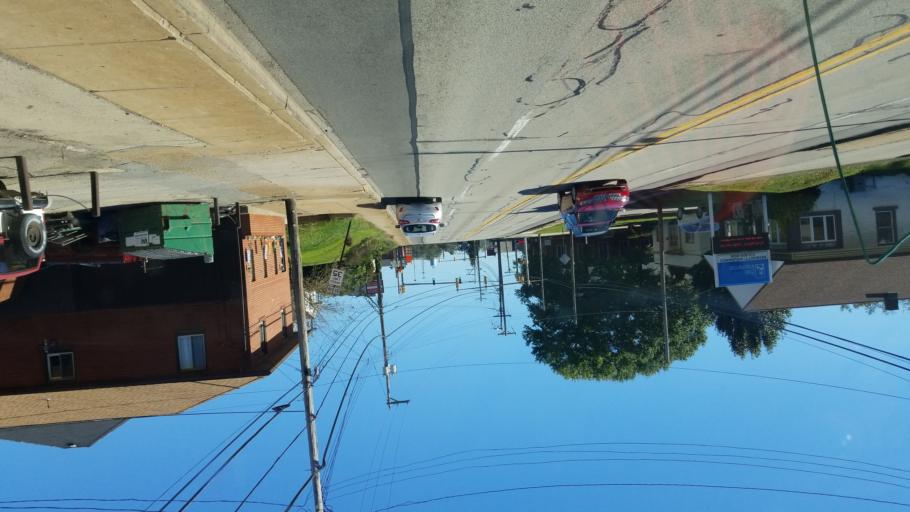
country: US
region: Pennsylvania
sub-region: Allegheny County
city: North Versailles
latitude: 40.3795
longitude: -79.8072
